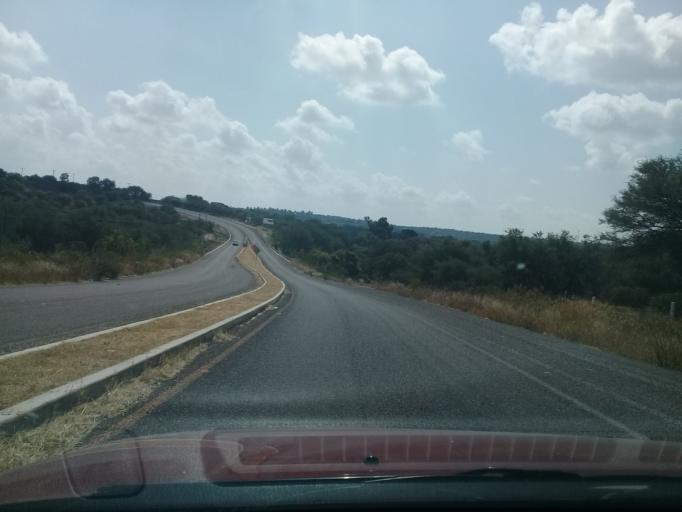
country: MX
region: Aguascalientes
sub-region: Aguascalientes
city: Penuelas (El Cienegal)
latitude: 21.7702
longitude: -102.3590
